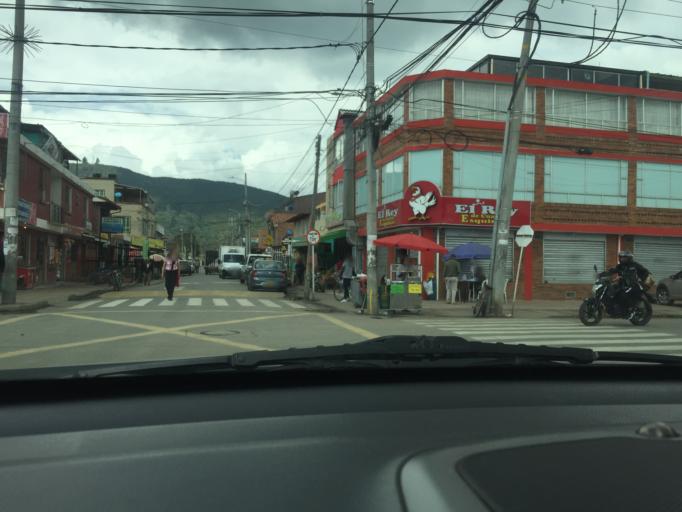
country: CO
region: Cundinamarca
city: Chia
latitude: 4.8738
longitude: -74.0663
